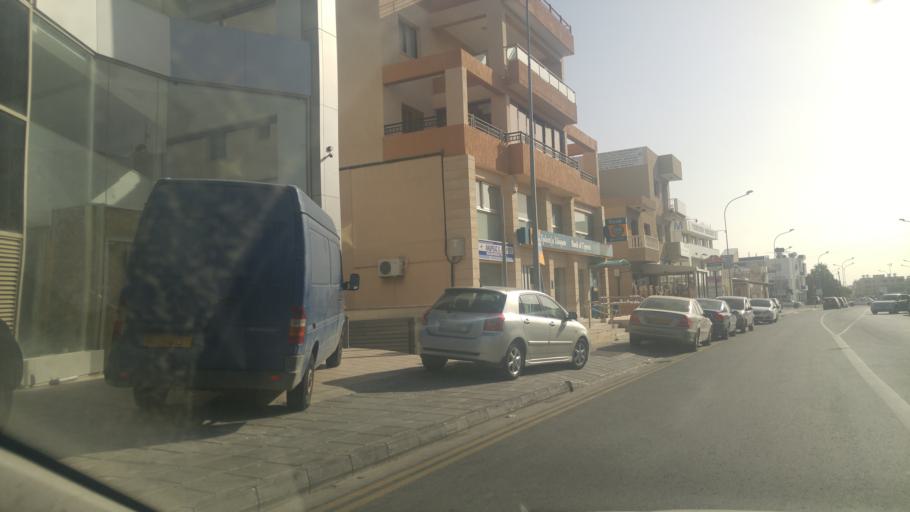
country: CY
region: Limassol
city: Pano Polemidia
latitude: 34.6884
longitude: 33.0104
